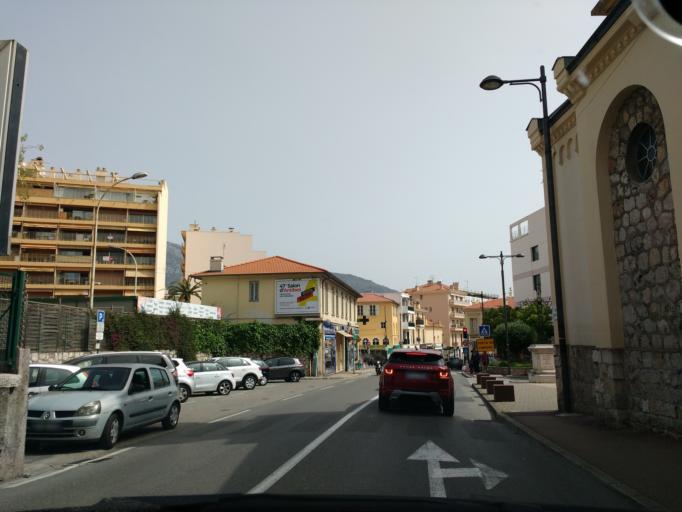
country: FR
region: Provence-Alpes-Cote d'Azur
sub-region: Departement des Alpes-Maritimes
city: Roquebrune-Cap-Martin
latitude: 43.7643
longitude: 7.4813
